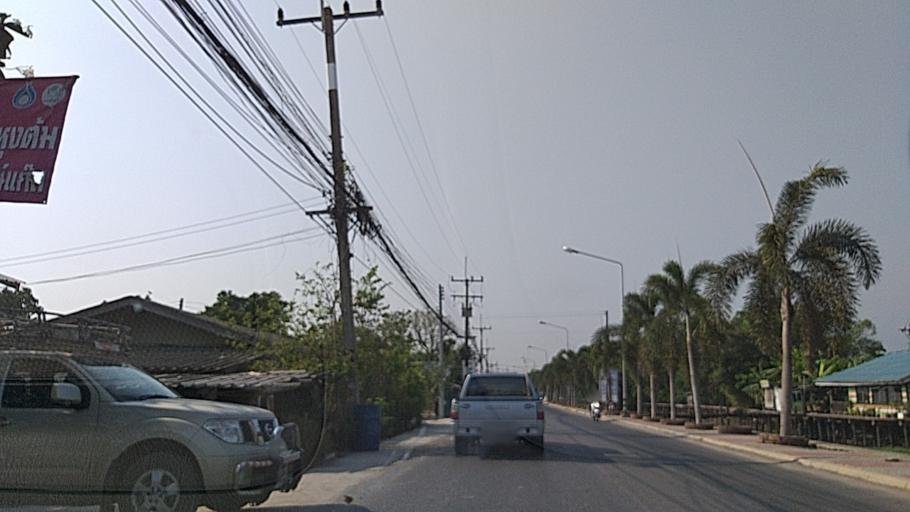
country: TH
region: Pathum Thani
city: Lam Luk Ka
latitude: 13.9372
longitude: 100.7061
